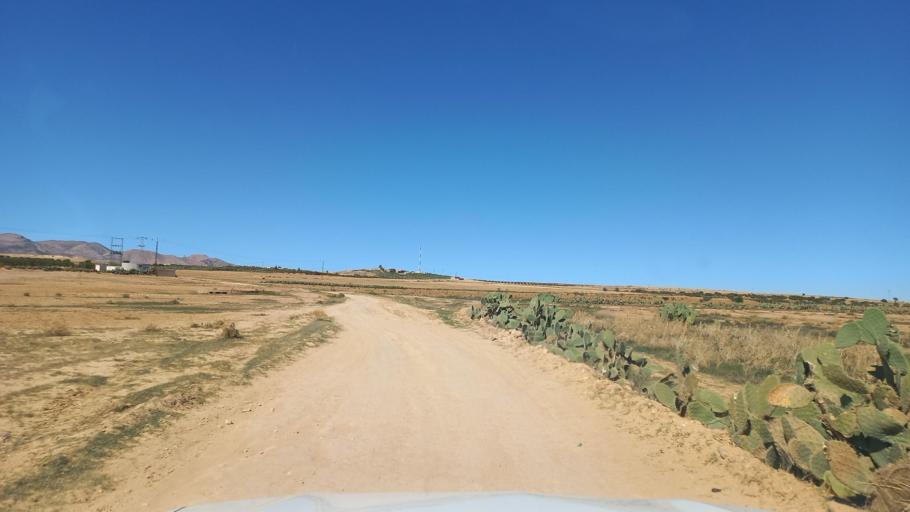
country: TN
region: Al Qasrayn
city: Sbiba
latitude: 35.3690
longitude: 9.0954
